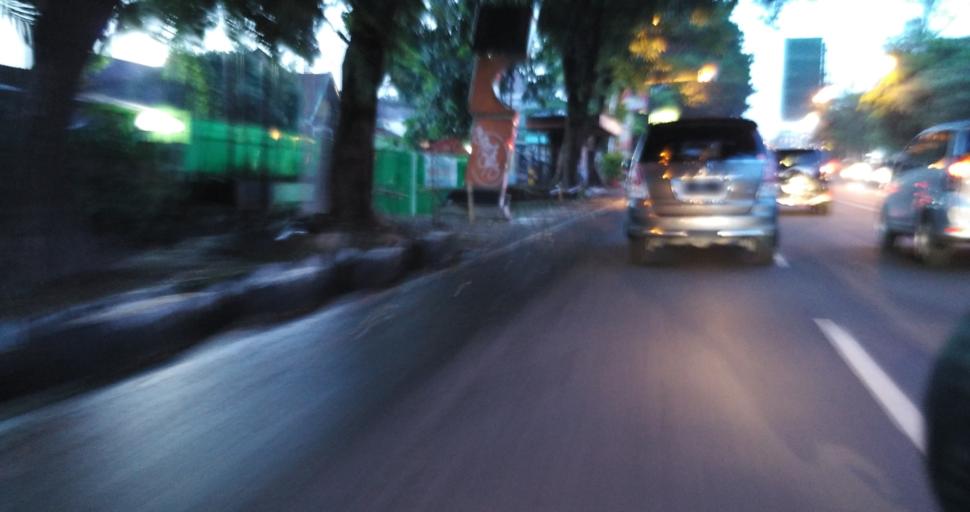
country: ID
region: Central Java
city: Semarang
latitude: -7.0174
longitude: 110.4187
